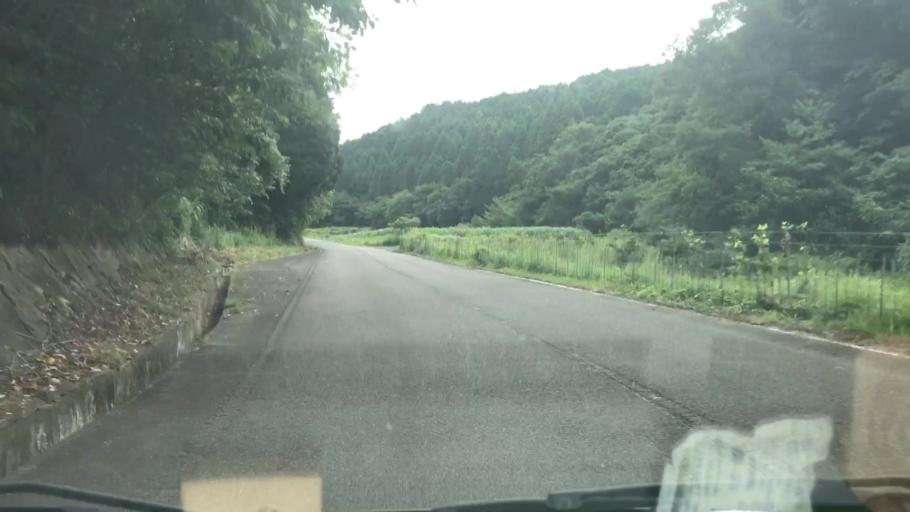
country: JP
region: Saga Prefecture
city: Takeocho-takeo
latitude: 33.2254
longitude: 129.9921
